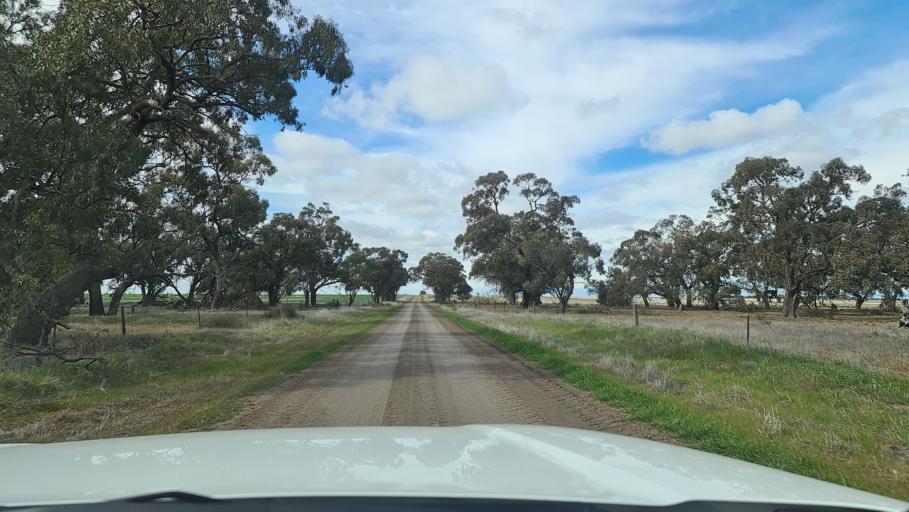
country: AU
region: Victoria
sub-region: Horsham
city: Horsham
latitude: -36.6313
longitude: 142.4145
